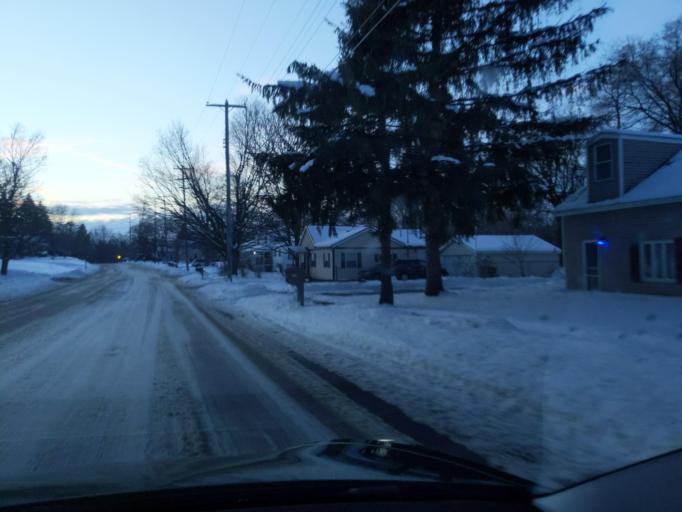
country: US
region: Michigan
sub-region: Ingham County
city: Mason
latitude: 42.5823
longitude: -84.4362
